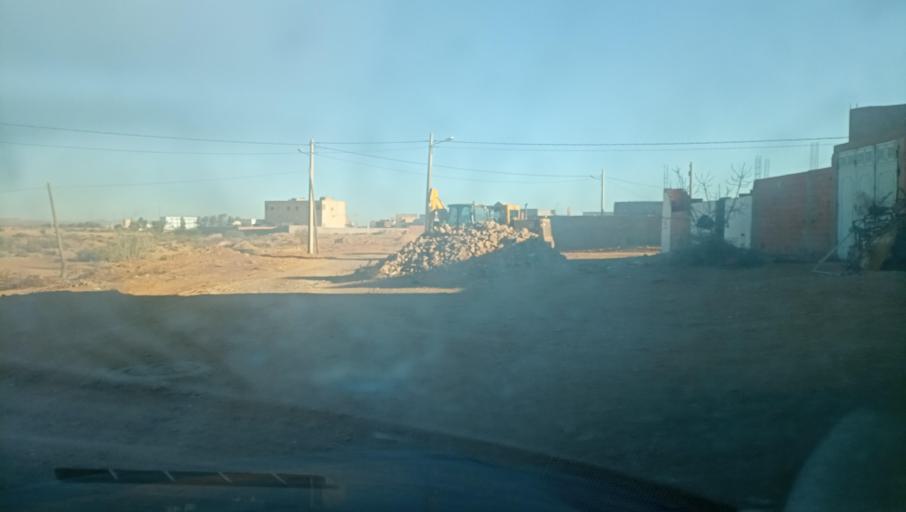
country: TN
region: Tataouine
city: Tataouine
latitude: 32.9880
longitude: 10.4572
